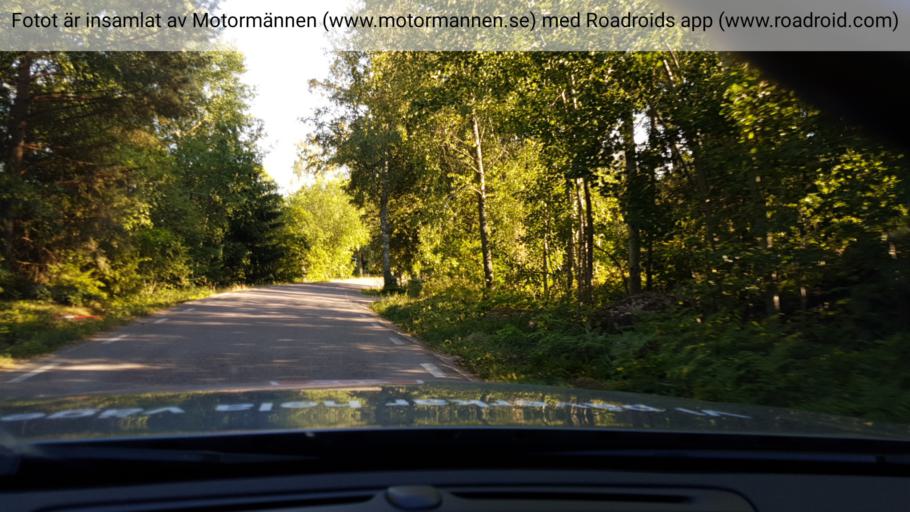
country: SE
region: Soedermanland
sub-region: Eskilstuna Kommun
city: Kvicksund
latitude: 59.5071
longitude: 16.3944
